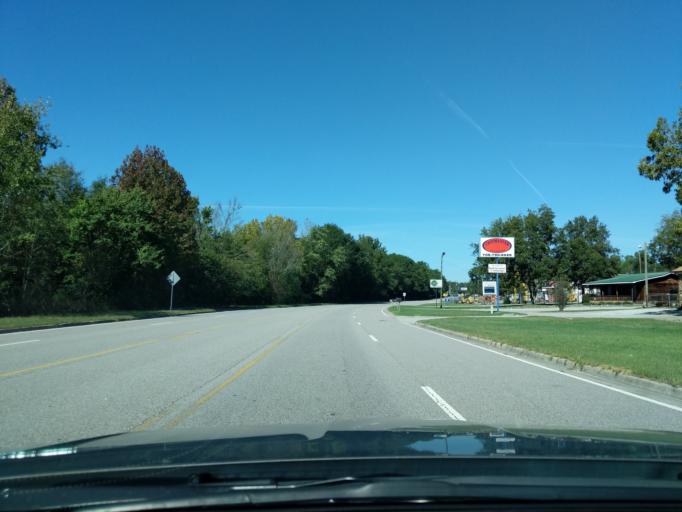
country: US
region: Georgia
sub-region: Richmond County
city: Augusta
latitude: 33.4309
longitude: -82.0071
